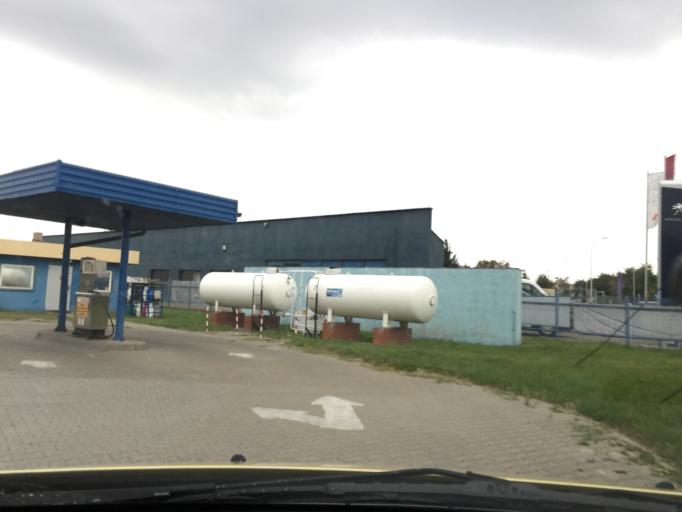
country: PL
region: Greater Poland Voivodeship
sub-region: Kalisz
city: Kalisz
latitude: 51.7425
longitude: 18.0626
